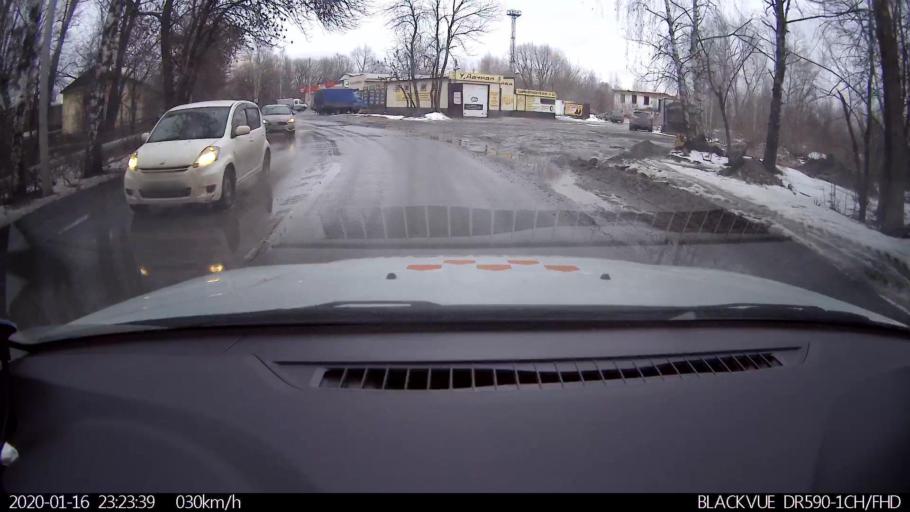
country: RU
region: Nizjnij Novgorod
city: Nizhniy Novgorod
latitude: 56.2995
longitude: 43.9123
